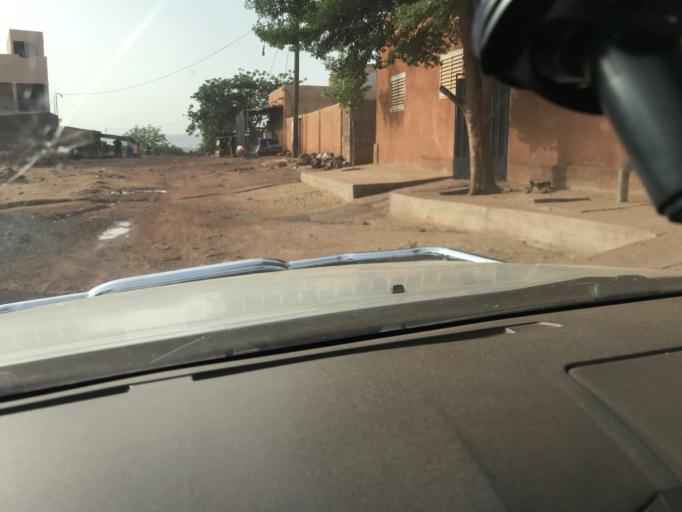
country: ML
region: Bamako
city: Bamako
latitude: 12.5900
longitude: -8.0083
